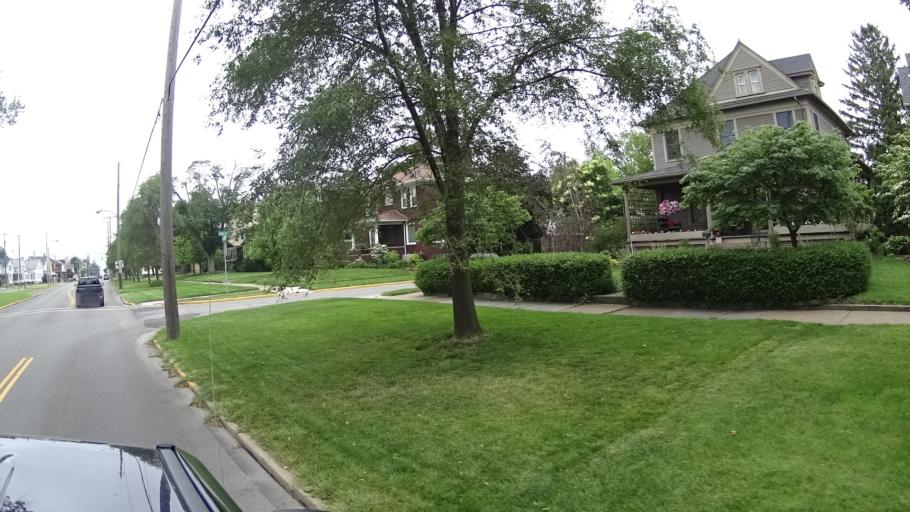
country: US
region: Ohio
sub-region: Erie County
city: Sandusky
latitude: 41.4453
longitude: -82.7052
